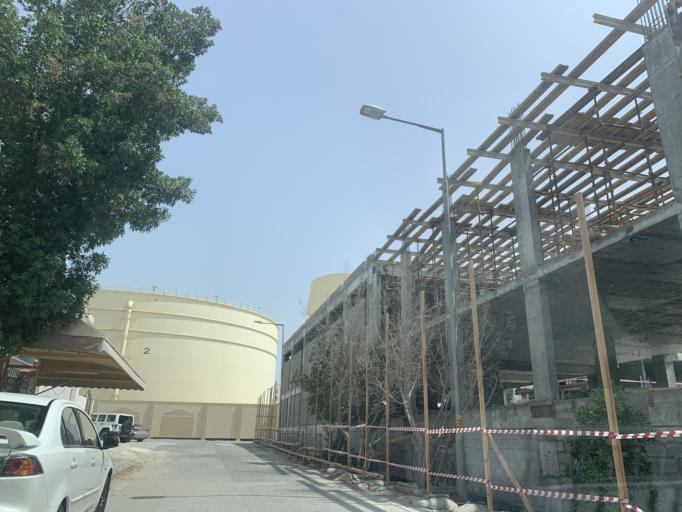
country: BH
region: Northern
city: Madinat `Isa
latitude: 26.1564
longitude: 50.5636
